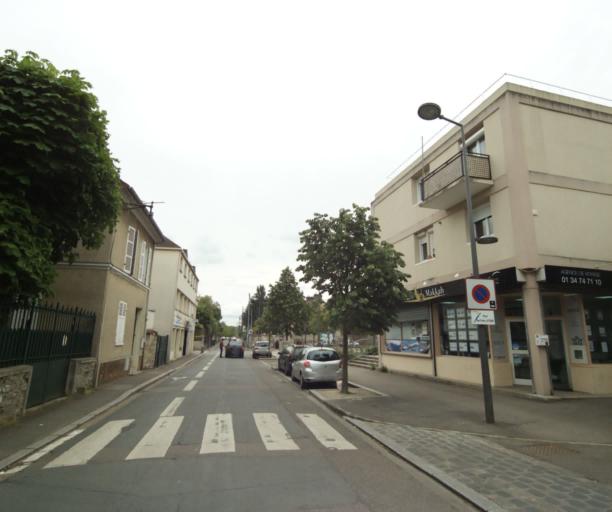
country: FR
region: Ile-de-France
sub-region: Departement des Yvelines
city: Les Mureaux
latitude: 48.9890
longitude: 1.9111
